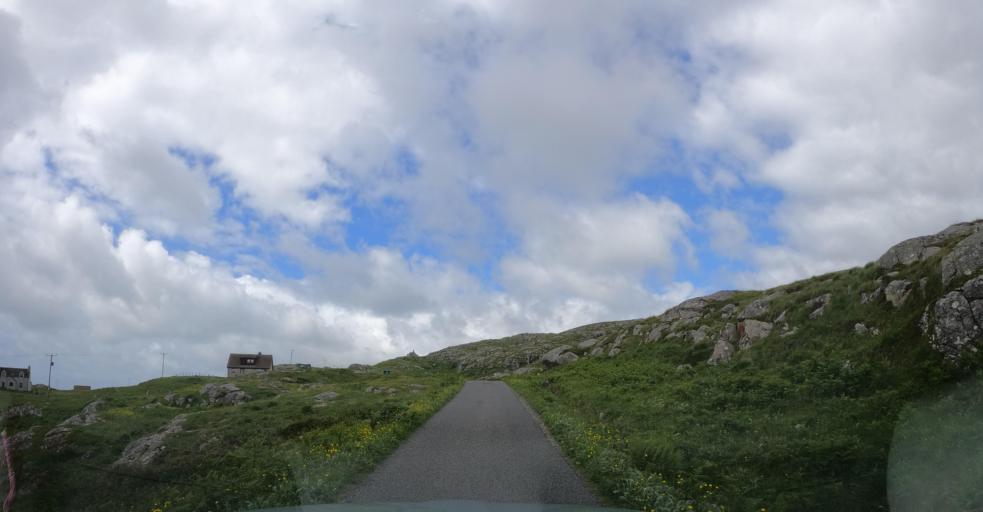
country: GB
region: Scotland
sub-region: Eilean Siar
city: Isle of South Uist
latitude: 57.0726
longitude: -7.2991
